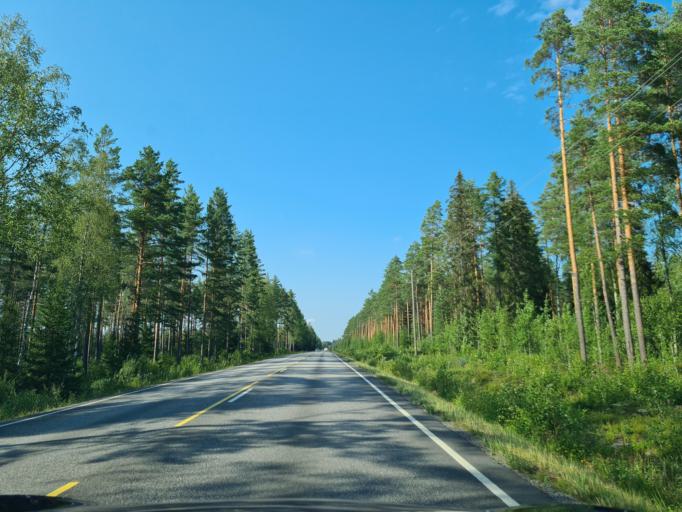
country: FI
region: Satakunta
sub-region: Pohjois-Satakunta
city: Kankaanpaeae
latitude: 61.9243
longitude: 22.5077
